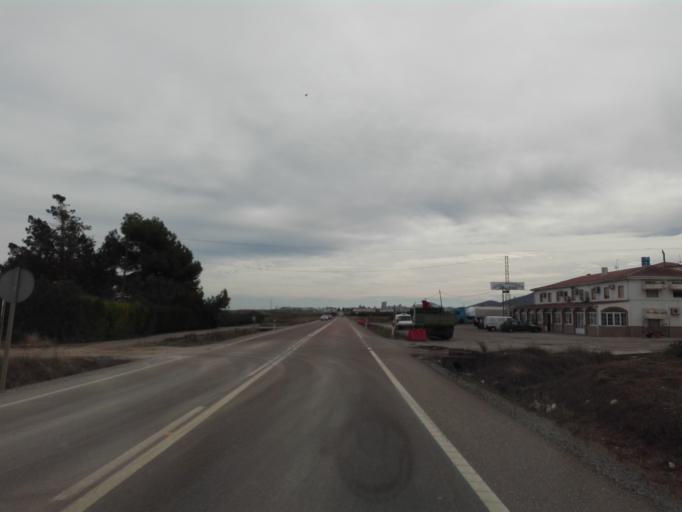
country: ES
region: Extremadura
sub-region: Provincia de Badajoz
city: Llerena
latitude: 38.2537
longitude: -6.0291
